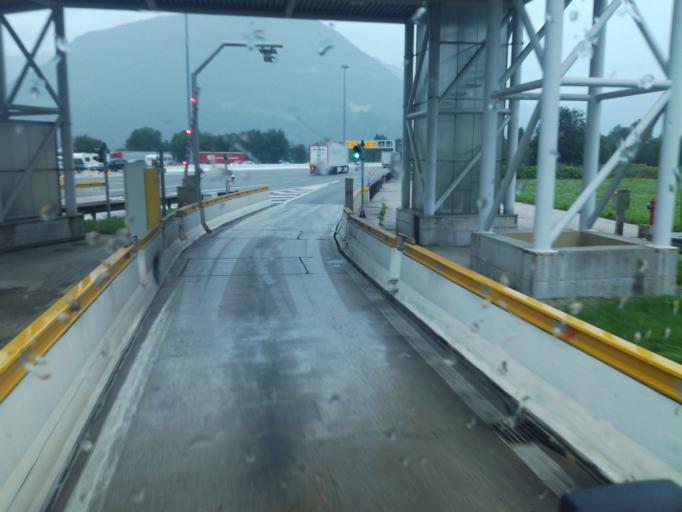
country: IT
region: Trentino-Alto Adige
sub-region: Bolzano
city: Vipiteno
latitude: 46.8846
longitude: 11.4344
